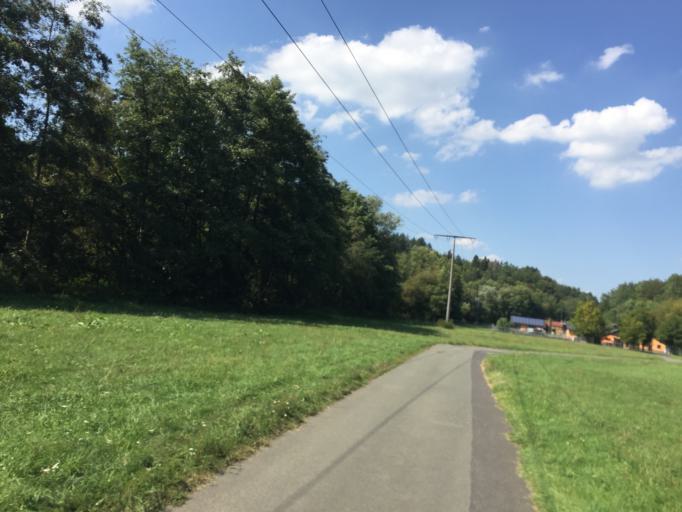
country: DE
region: Hesse
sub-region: Regierungsbezirk Giessen
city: Braunfels
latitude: 50.5049
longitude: 8.4201
